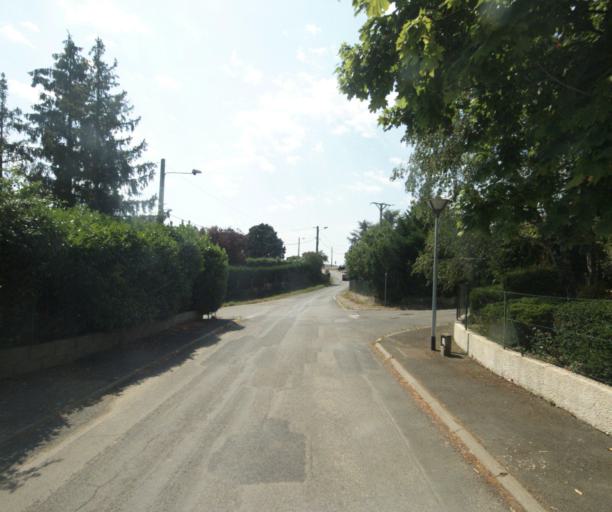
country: FR
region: Rhone-Alpes
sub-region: Departement du Rhone
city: Lentilly
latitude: 45.8443
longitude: 4.6595
